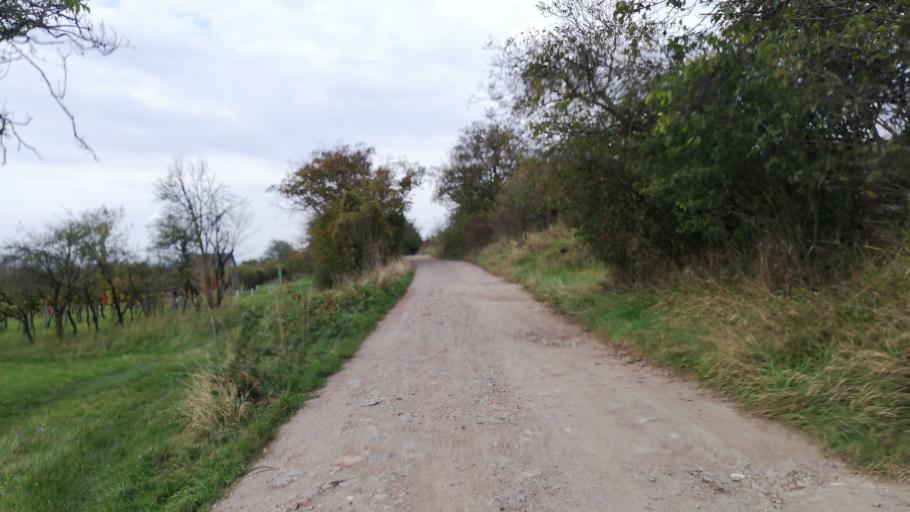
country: SK
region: Trnavsky
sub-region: Okres Skalica
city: Skalica
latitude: 48.8219
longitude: 17.2370
